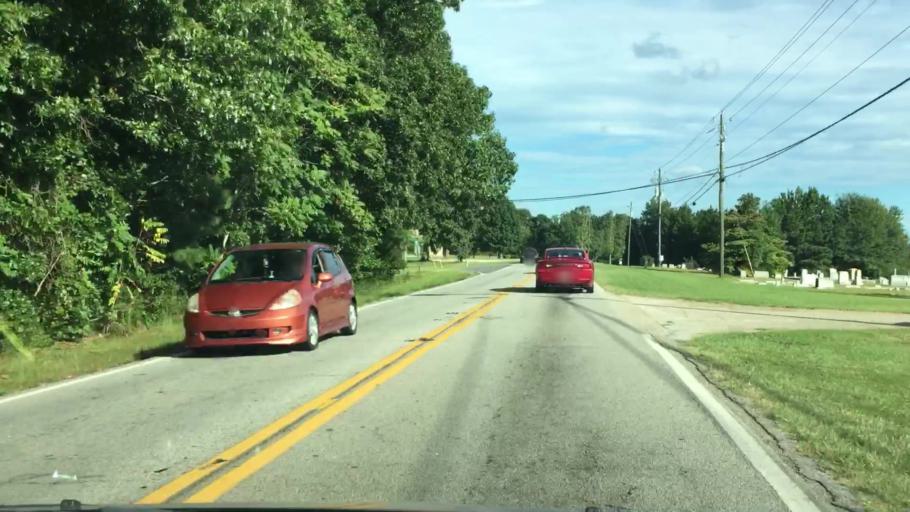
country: US
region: Georgia
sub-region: Henry County
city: Stockbridge
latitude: 33.6160
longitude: -84.2326
